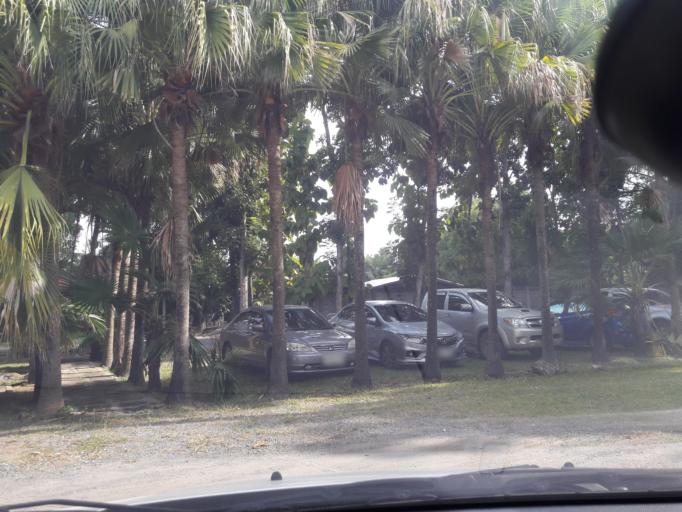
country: TH
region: Chiang Mai
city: San Kamphaeng
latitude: 18.7756
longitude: 99.1199
